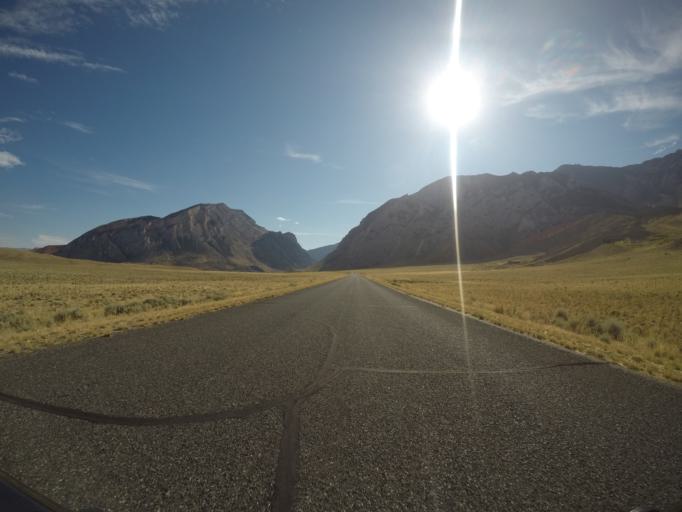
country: US
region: Montana
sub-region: Carbon County
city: Red Lodge
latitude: 44.8661
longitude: -109.2795
